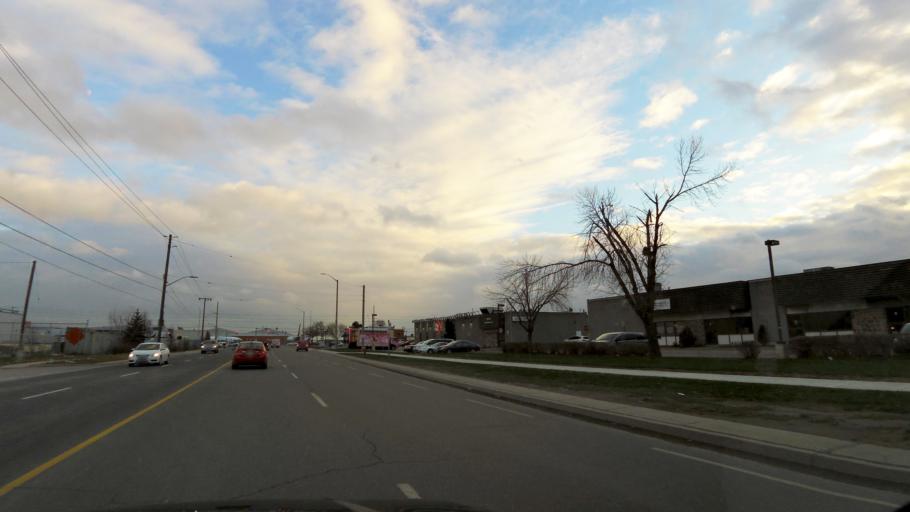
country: CA
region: Ontario
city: Etobicoke
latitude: 43.6958
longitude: -79.6548
